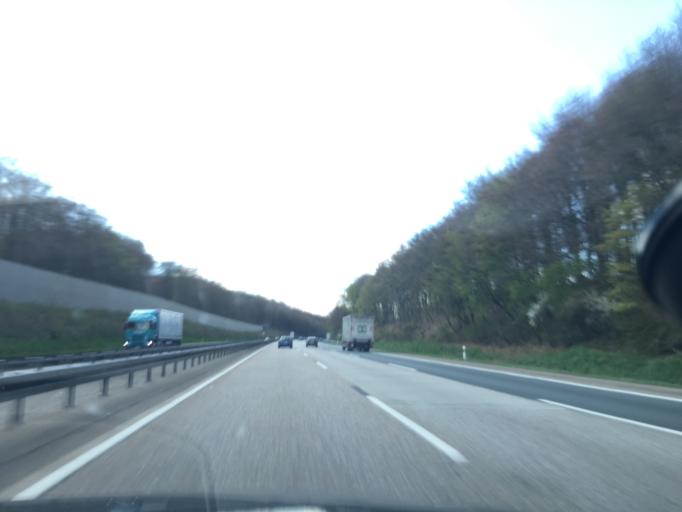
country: DE
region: North Rhine-Westphalia
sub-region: Regierungsbezirk Arnsberg
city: Siegen
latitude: 50.8663
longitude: 7.9739
